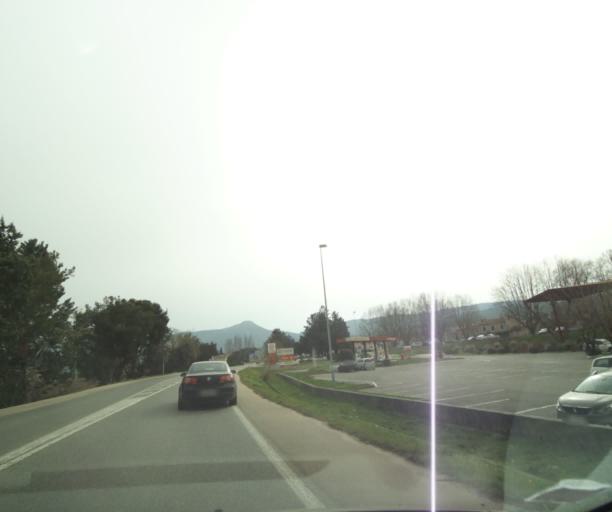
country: FR
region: Provence-Alpes-Cote d'Azur
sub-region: Departement des Bouches-du-Rhone
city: Trets
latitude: 43.4503
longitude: 5.6864
